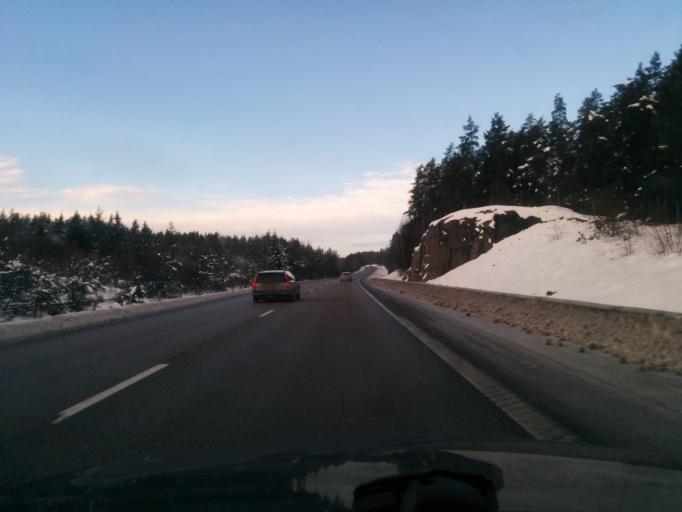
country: SE
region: Stockholm
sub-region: Upplands-Bro Kommun
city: Bro
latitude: 59.5475
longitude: 17.5986
